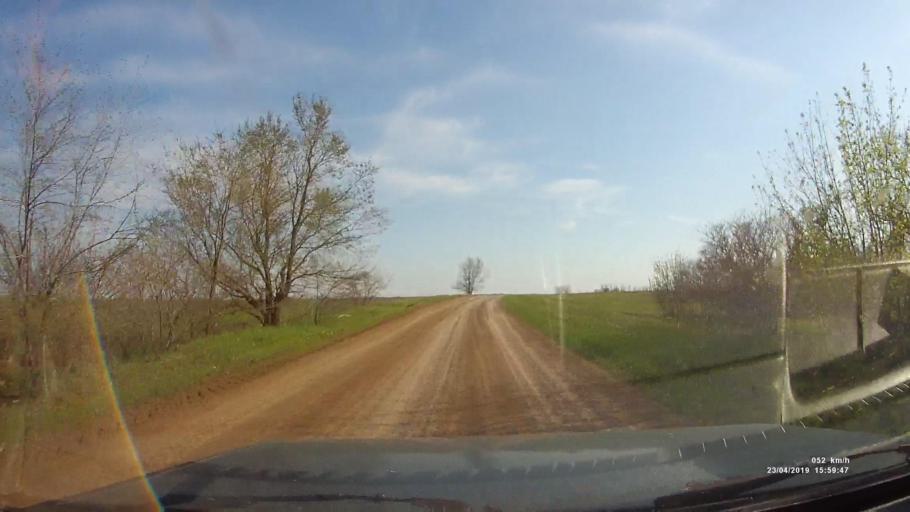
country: RU
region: Rostov
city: Remontnoye
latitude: 46.5141
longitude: 43.1095
